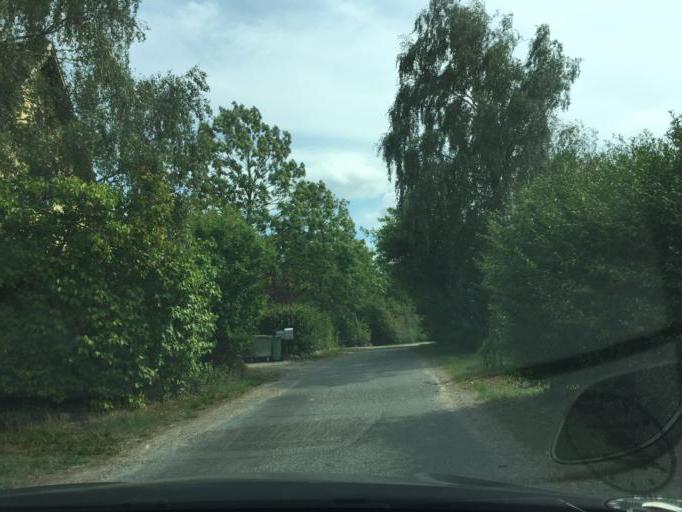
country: DK
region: South Denmark
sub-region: Assens Kommune
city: Tommerup Stationsby
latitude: 55.4036
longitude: 10.2347
